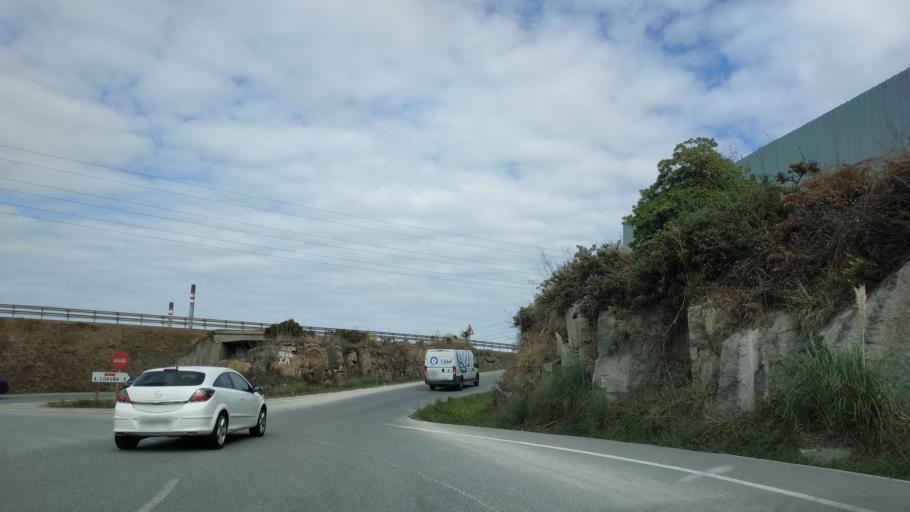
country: ES
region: Galicia
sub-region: Provincia da Coruna
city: A Coruna
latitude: 43.3419
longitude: -8.4437
